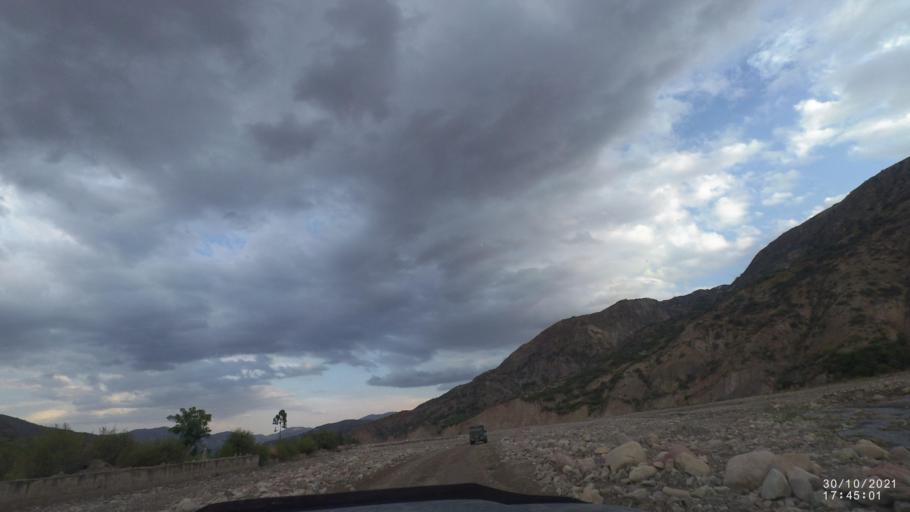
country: BO
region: Cochabamba
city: Sipe Sipe
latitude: -17.5298
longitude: -66.5325
